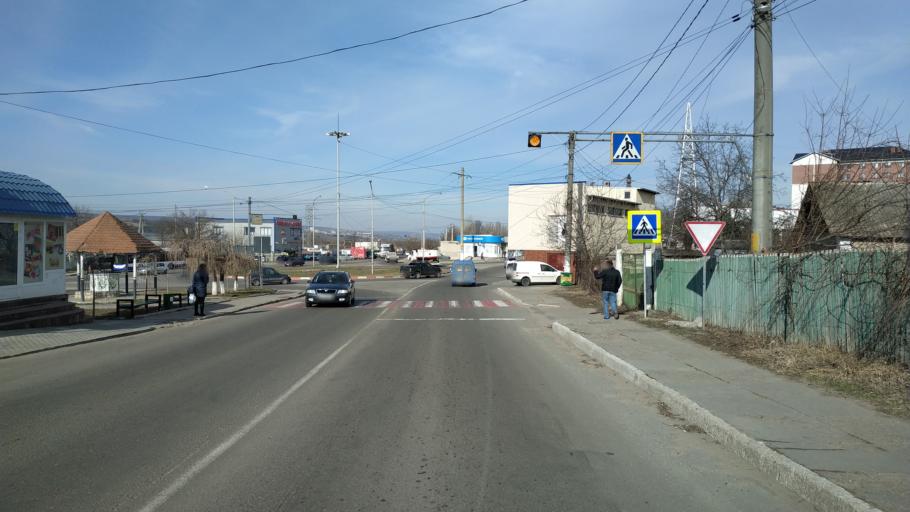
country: MD
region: Laloveni
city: Ialoveni
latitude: 46.9435
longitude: 28.7778
